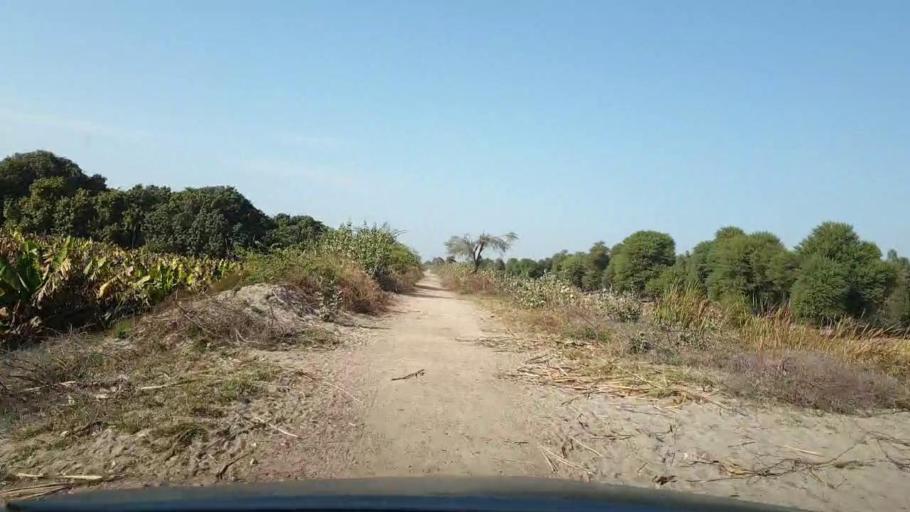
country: PK
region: Sindh
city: Tando Adam
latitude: 25.6047
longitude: 68.6245
